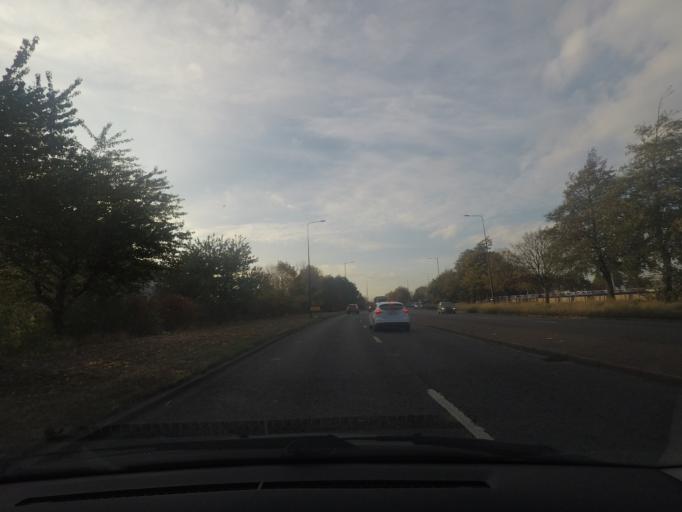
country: GB
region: England
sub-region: North East Lincolnshire
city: Grimbsy
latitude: 53.5742
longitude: -0.0939
